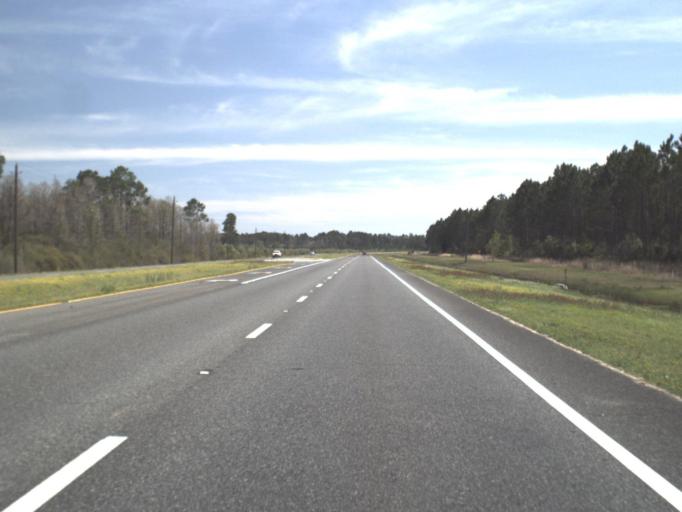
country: US
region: Florida
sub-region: Bay County
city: Lynn Haven
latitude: 30.3464
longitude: -85.6630
